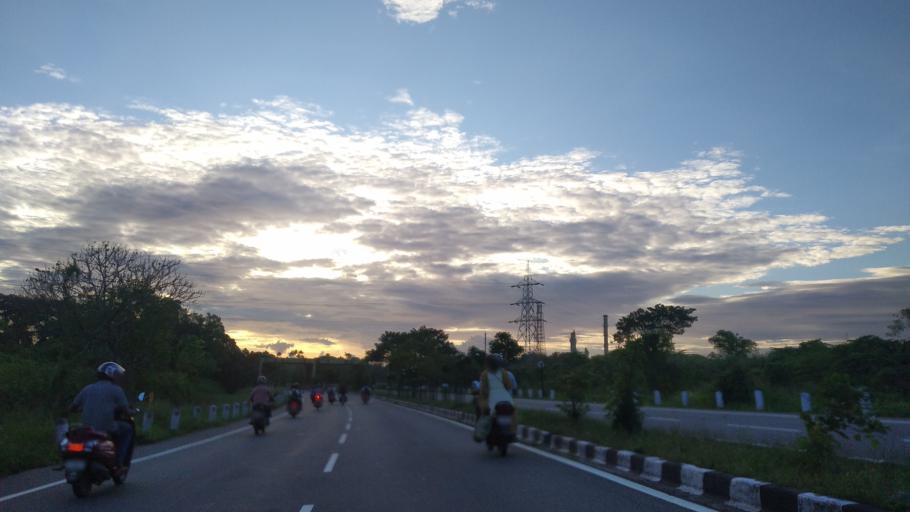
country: IN
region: Kerala
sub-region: Ernakulam
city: Elur
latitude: 10.0696
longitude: 76.3040
